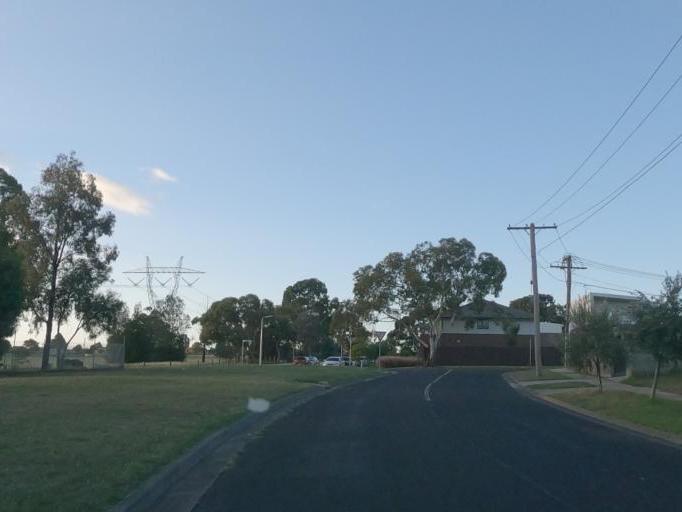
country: AU
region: Victoria
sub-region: Hume
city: Jacana
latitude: -37.6753
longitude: 144.9052
